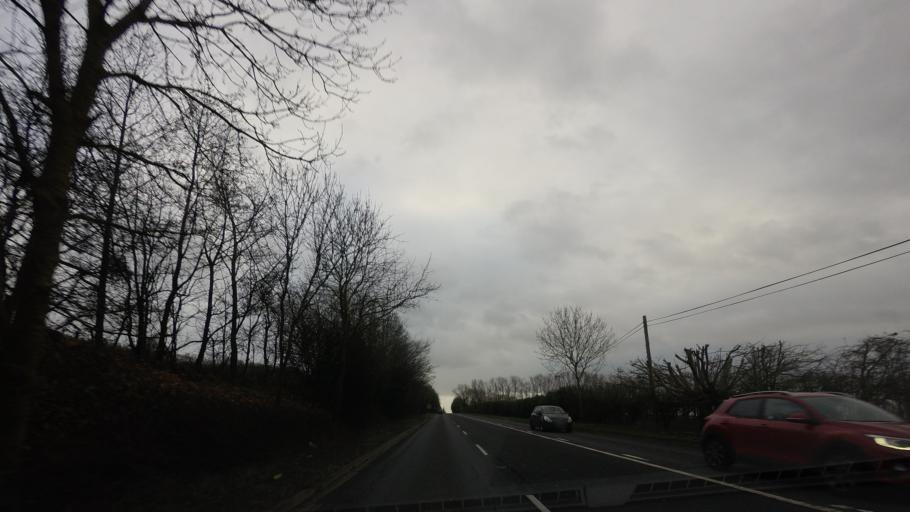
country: GB
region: England
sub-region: Kent
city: East Peckham
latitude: 51.2484
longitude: 0.3745
